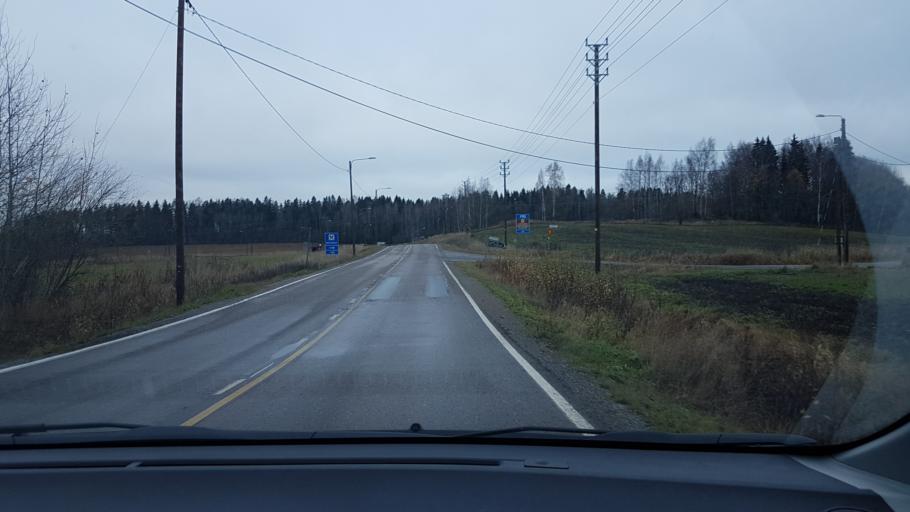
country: FI
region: Uusimaa
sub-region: Helsinki
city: Vantaa
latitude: 60.2759
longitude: 25.1370
